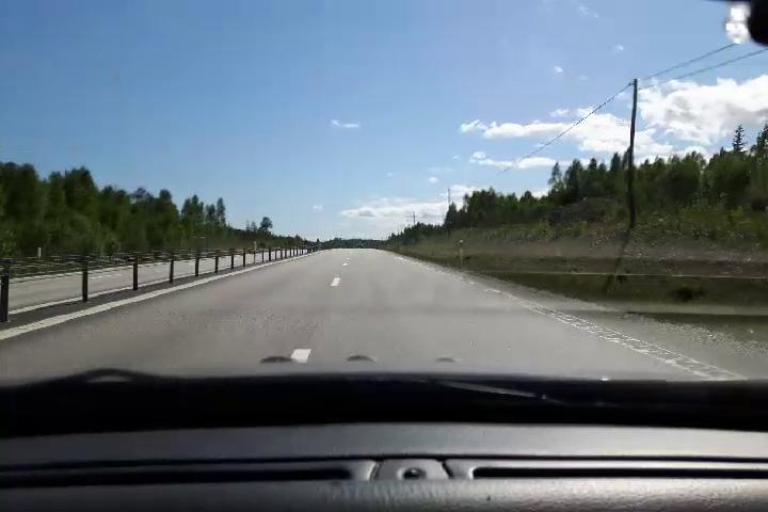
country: SE
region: Gaevleborg
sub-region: Hudiksvalls Kommun
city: Iggesund
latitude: 61.6771
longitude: 17.0352
